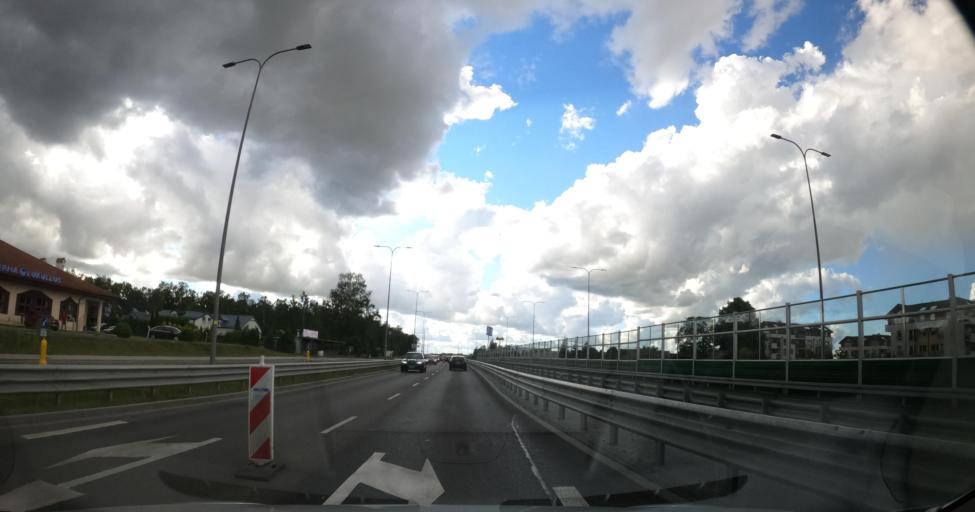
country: PL
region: Pomeranian Voivodeship
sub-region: Powiat gdanski
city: Lublewo Gdanskie
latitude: 54.3524
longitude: 18.4997
